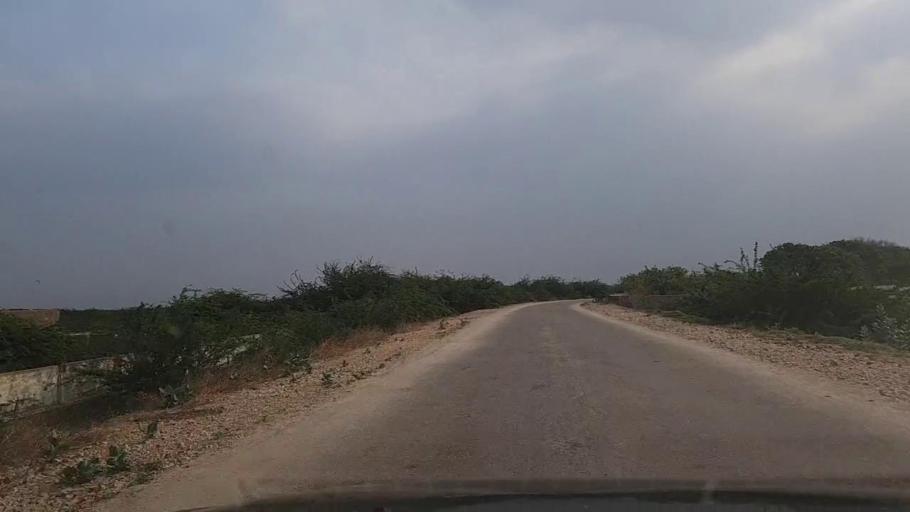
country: PK
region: Sindh
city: Thatta
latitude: 24.8543
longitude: 67.7783
